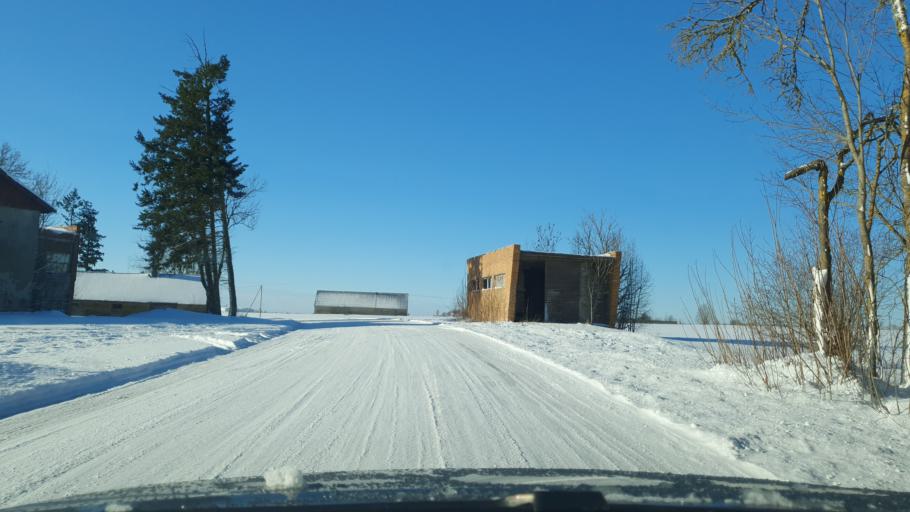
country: EE
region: Harju
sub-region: Kuusalu vald
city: Kuusalu
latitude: 59.4596
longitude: 25.4131
